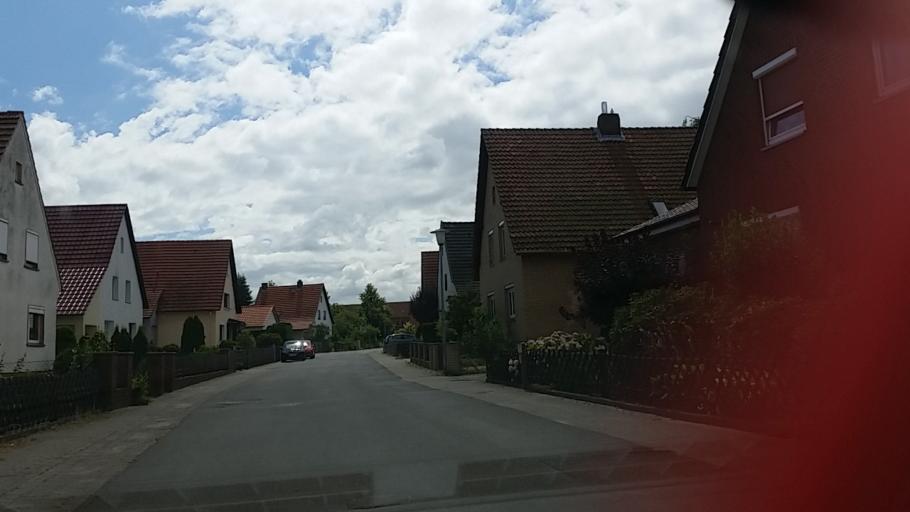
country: DE
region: Lower Saxony
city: Wolfsburg
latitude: 52.4226
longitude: 10.8193
